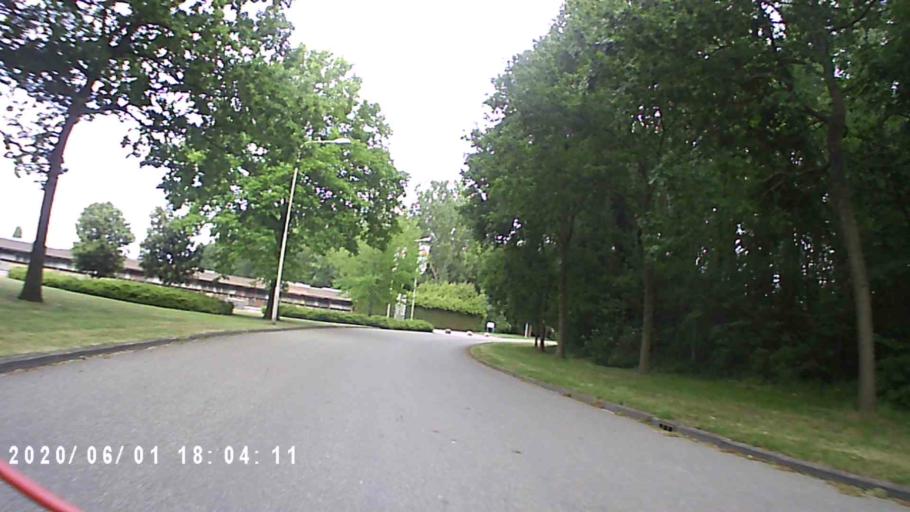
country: NL
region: Friesland
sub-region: Gemeente Tytsjerksteradiel
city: Sumar
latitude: 53.1833
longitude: 5.9929
